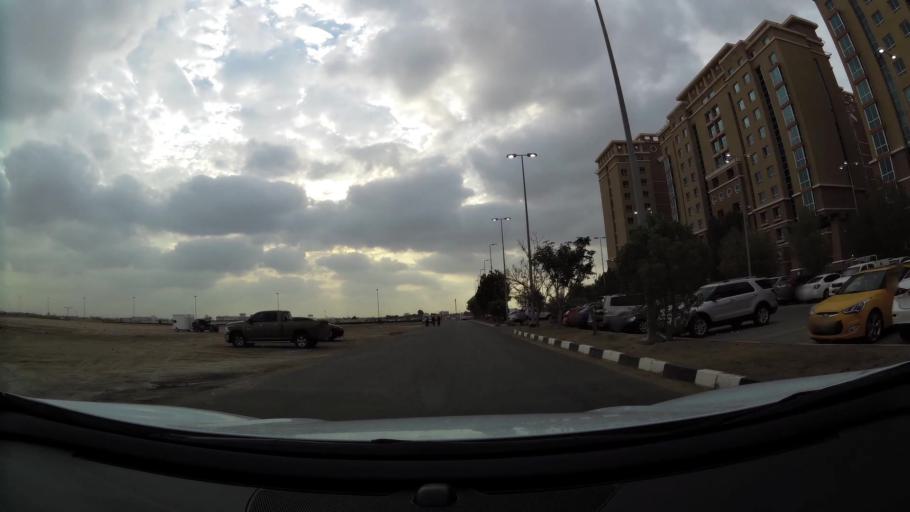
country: AE
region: Abu Dhabi
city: Abu Dhabi
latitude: 24.3701
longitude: 54.5387
